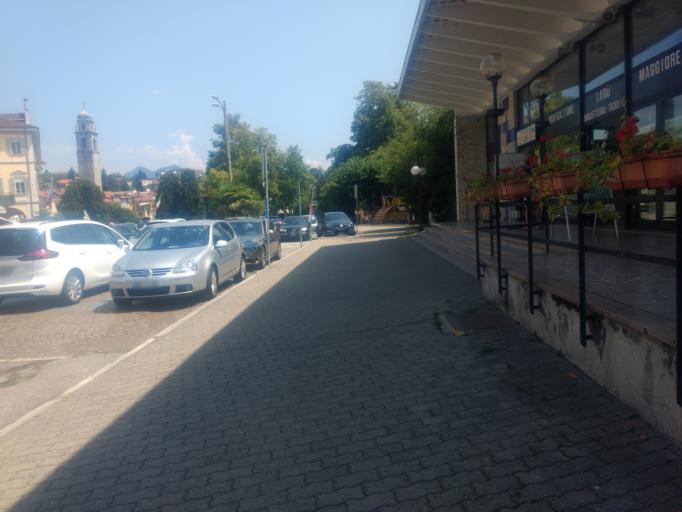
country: IT
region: Piedmont
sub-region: Provincia Verbano-Cusio-Ossola
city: Verbania
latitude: 45.9212
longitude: 8.5499
